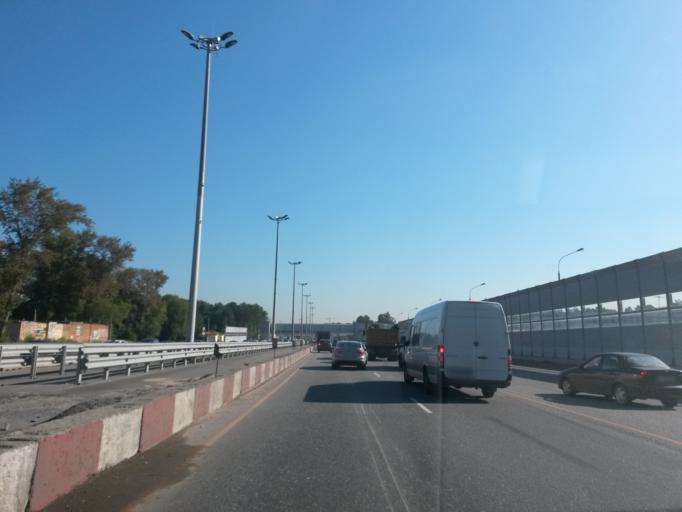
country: RU
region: Moskovskaya
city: Bolshevo
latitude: 55.9324
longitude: 37.8062
